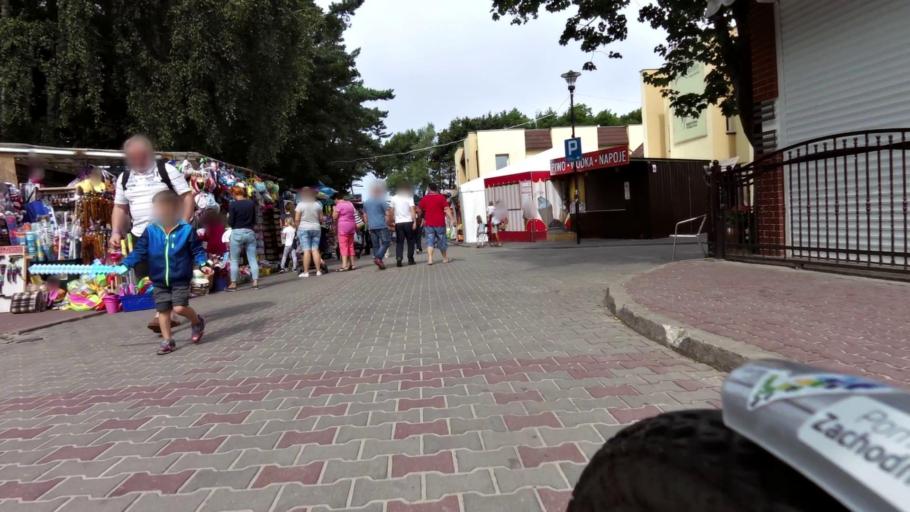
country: PL
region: West Pomeranian Voivodeship
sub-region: Powiat kolobrzeski
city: Ustronie Morskie
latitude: 54.2139
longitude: 15.7451
